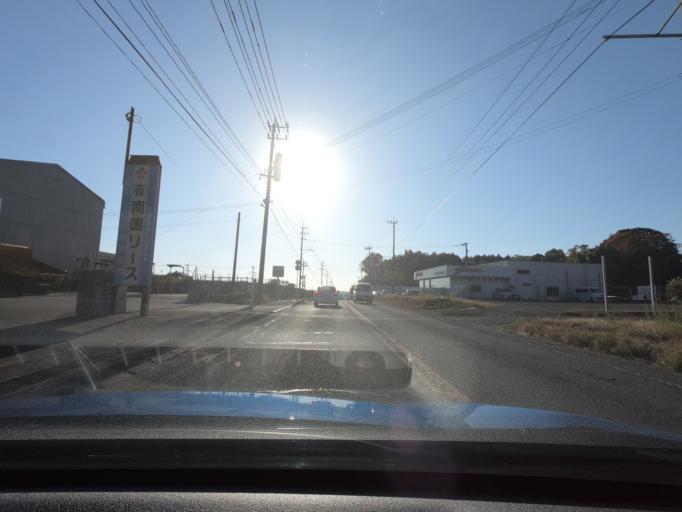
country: JP
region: Kagoshima
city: Akune
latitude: 32.0756
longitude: 130.2523
